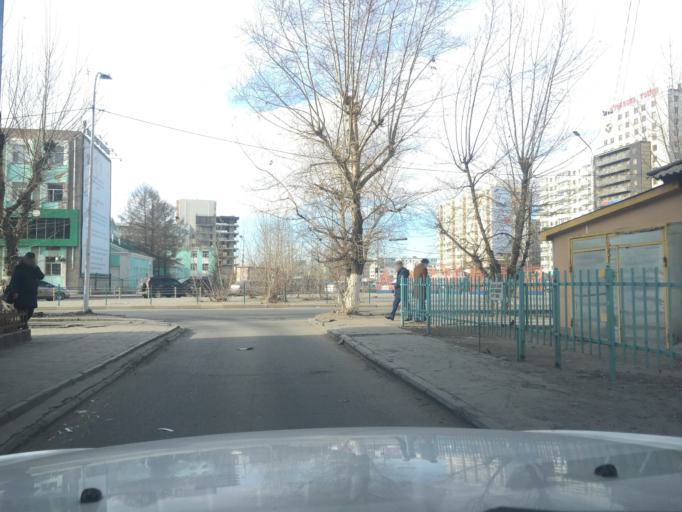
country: MN
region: Ulaanbaatar
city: Ulaanbaatar
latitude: 47.9140
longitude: 106.8779
